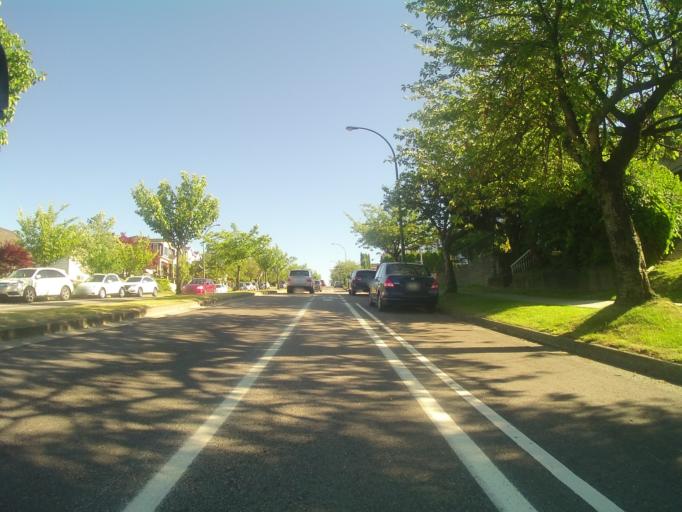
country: CA
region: British Columbia
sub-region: Fraser Valley Regional District
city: North Vancouver
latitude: 49.2560
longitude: -123.0339
